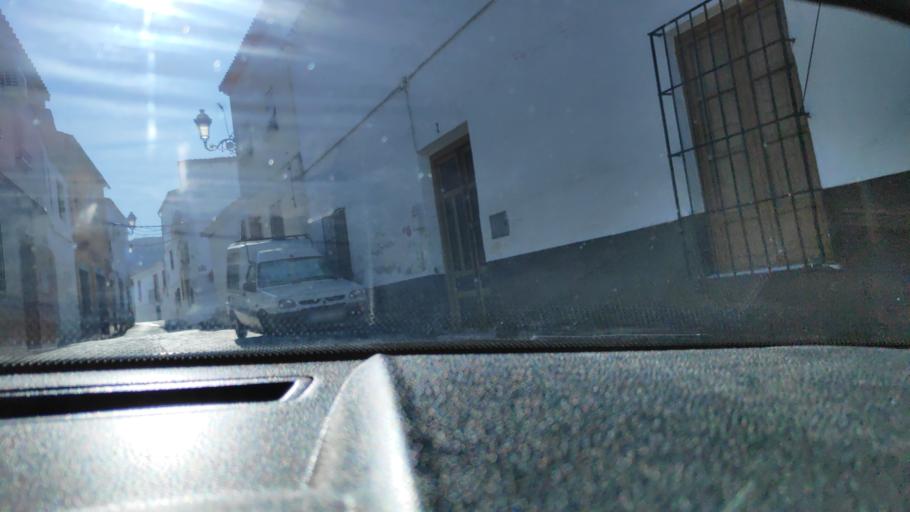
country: ES
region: Andalusia
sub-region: Province of Cordoba
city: Baena
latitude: 37.6140
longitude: -4.3342
